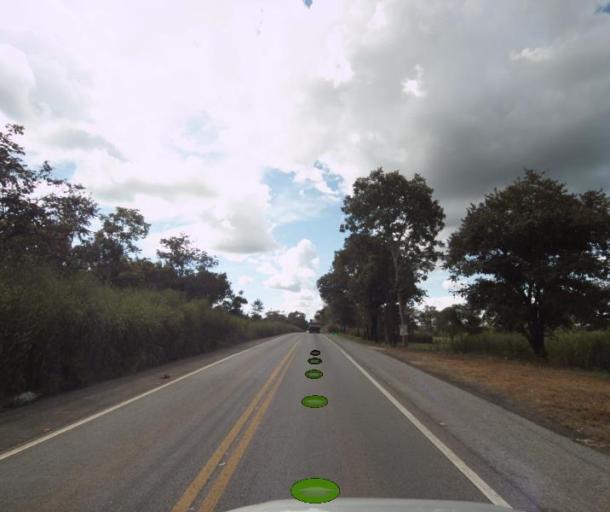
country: BR
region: Goias
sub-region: Porangatu
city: Porangatu
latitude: -13.1579
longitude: -49.1798
